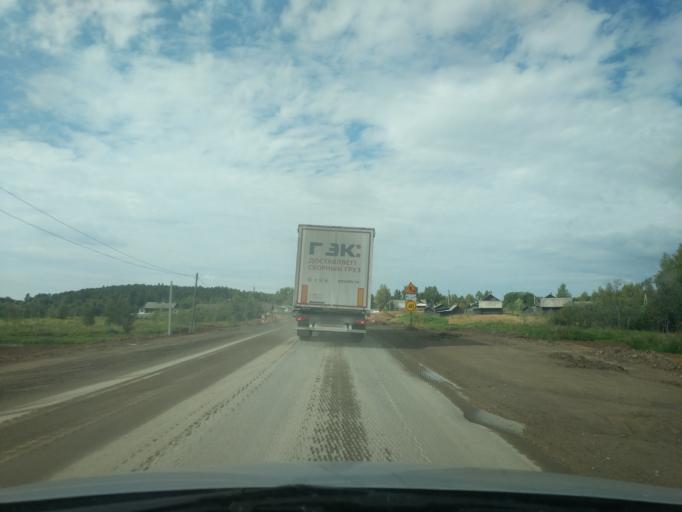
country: RU
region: Kostroma
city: Sudislavl'
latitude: 57.8760
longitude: 41.7315
